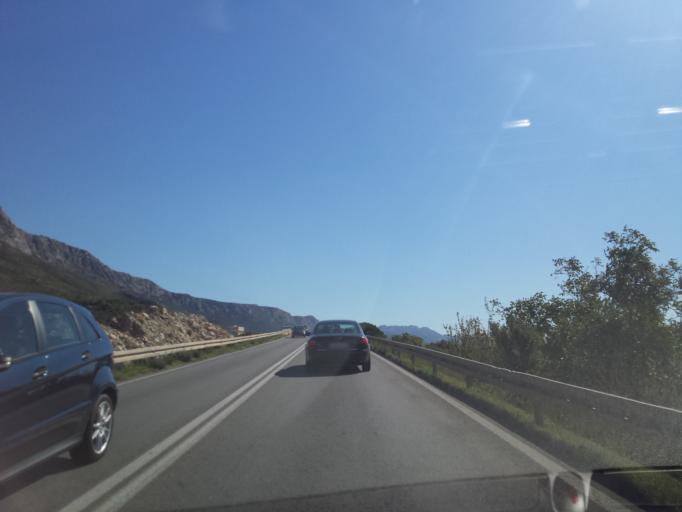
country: HR
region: Splitsko-Dalmatinska
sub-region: Grad Split
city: Split
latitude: 43.5572
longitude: 16.3776
